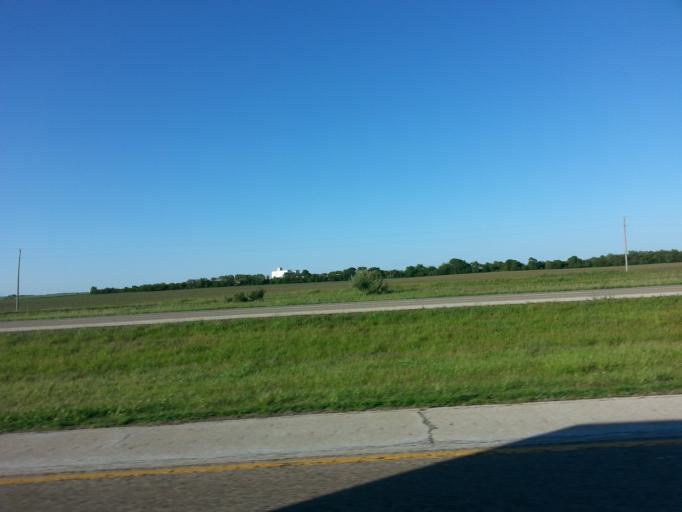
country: US
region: Illinois
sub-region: McLean County
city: Le Roy
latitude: 40.3047
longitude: -88.7182
